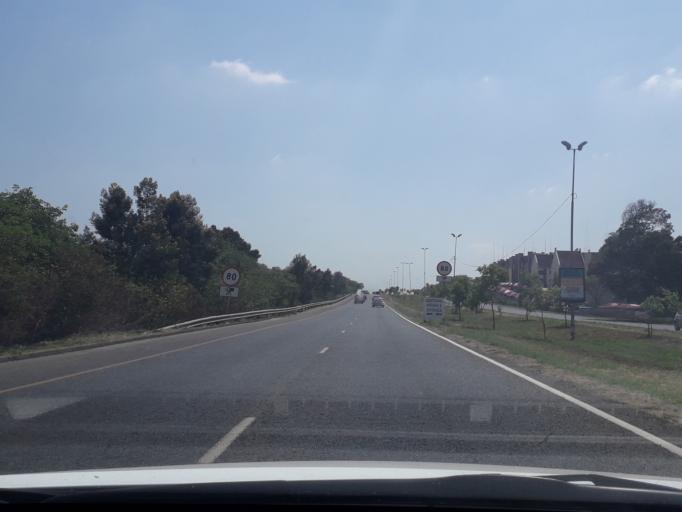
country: ZA
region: Gauteng
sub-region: West Rand District Municipality
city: Muldersdriseloop
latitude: -26.0706
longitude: 27.9377
